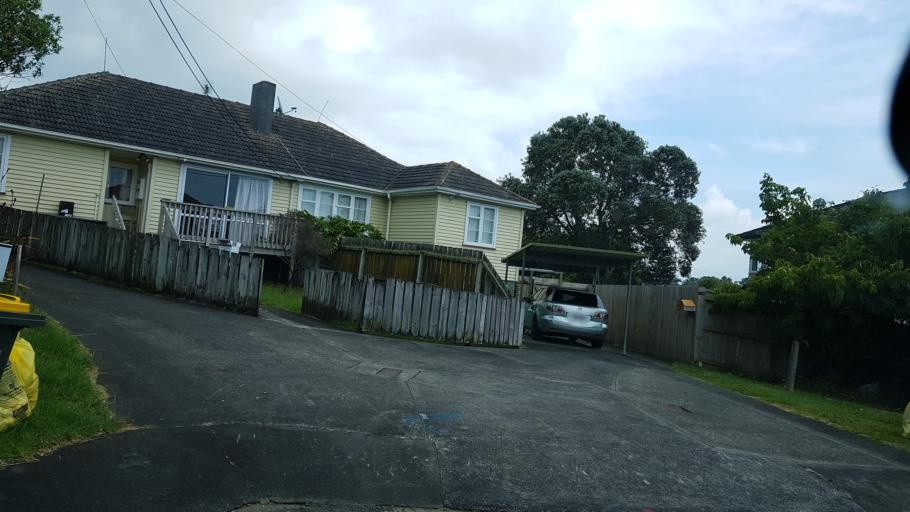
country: NZ
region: Auckland
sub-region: Auckland
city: North Shore
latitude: -36.8061
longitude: 174.7875
